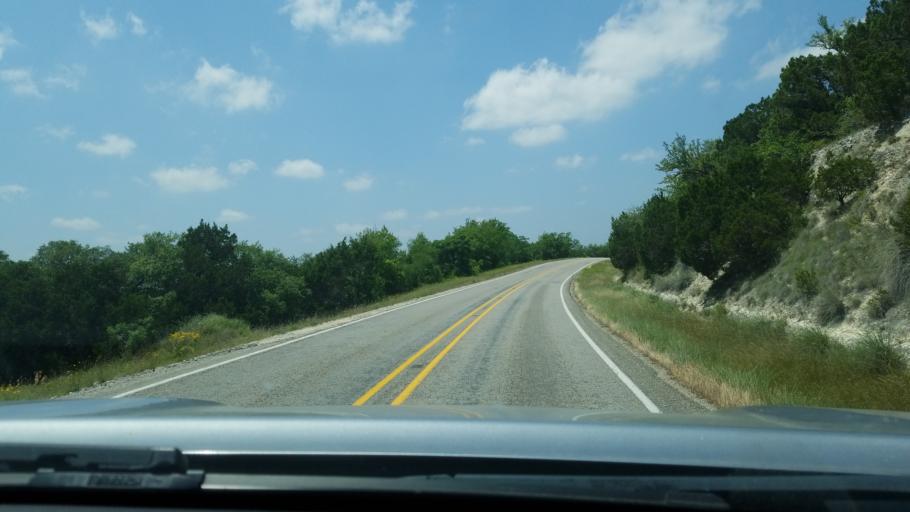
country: US
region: Texas
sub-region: Hays County
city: Woodcreek
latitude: 30.0937
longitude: -98.2342
